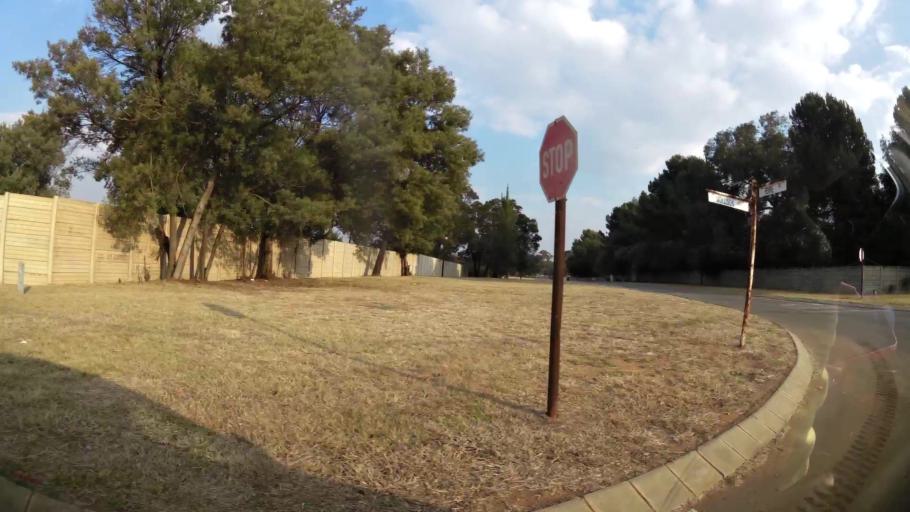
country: ZA
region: Gauteng
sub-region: Ekurhuleni Metropolitan Municipality
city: Benoni
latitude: -26.1251
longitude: 28.3040
